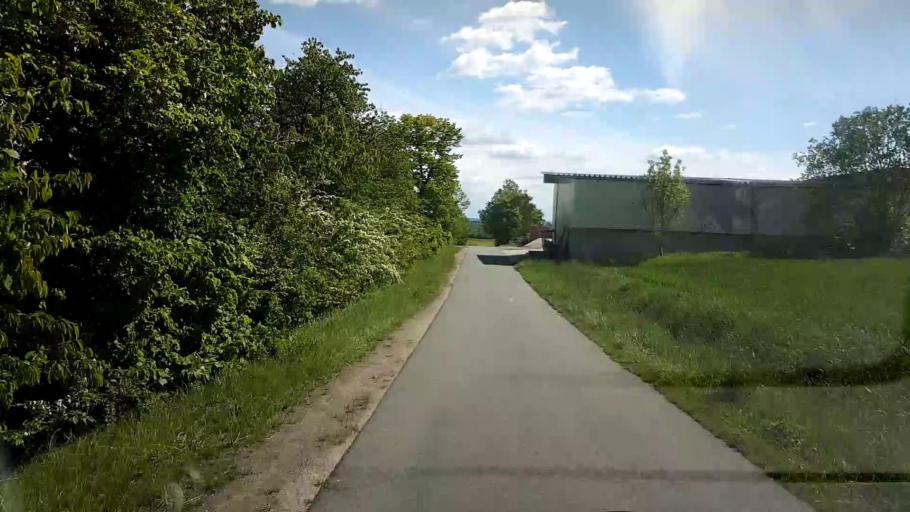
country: DE
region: Bavaria
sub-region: Upper Franconia
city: Buttenheim
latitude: 49.8105
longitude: 11.0391
